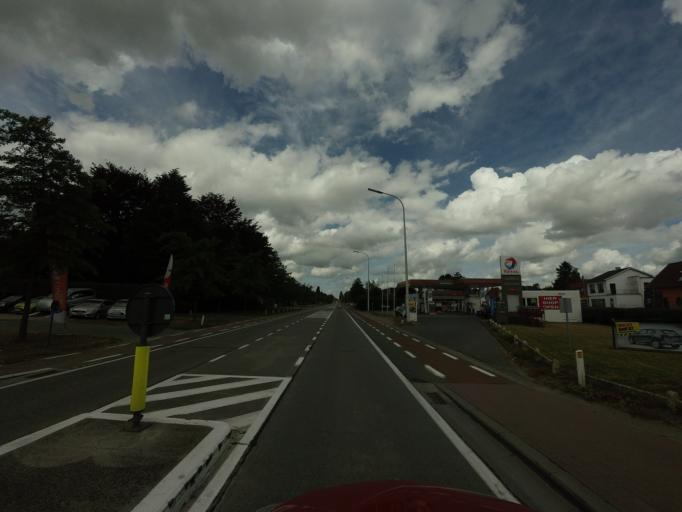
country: BE
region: Flanders
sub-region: Provincie Oost-Vlaanderen
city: Eeklo
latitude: 51.1996
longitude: 3.5272
